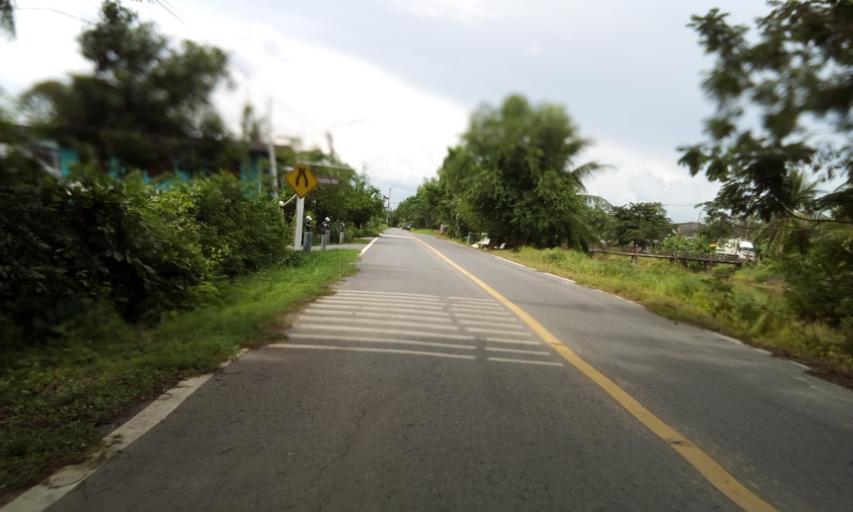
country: TH
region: Pathum Thani
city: Nong Suea
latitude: 14.1245
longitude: 100.8235
